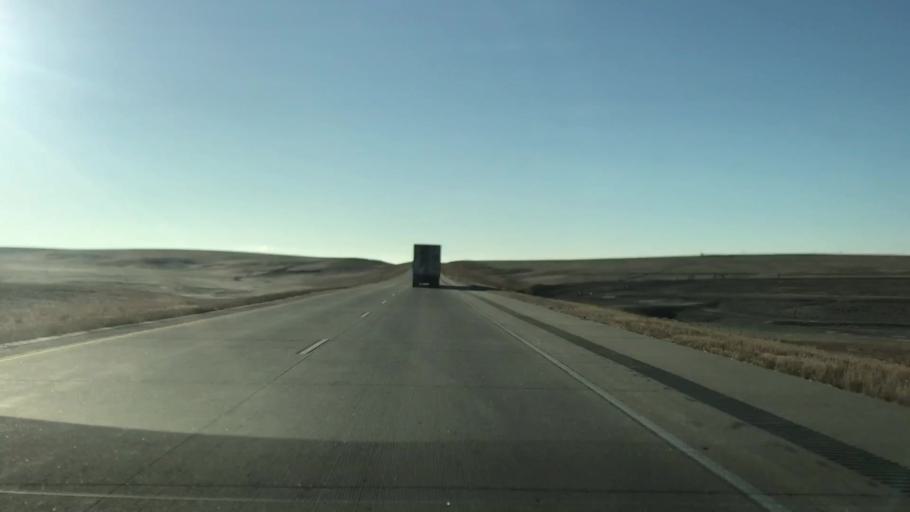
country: US
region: Colorado
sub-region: Lincoln County
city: Limon
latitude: 39.3995
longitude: -103.8990
